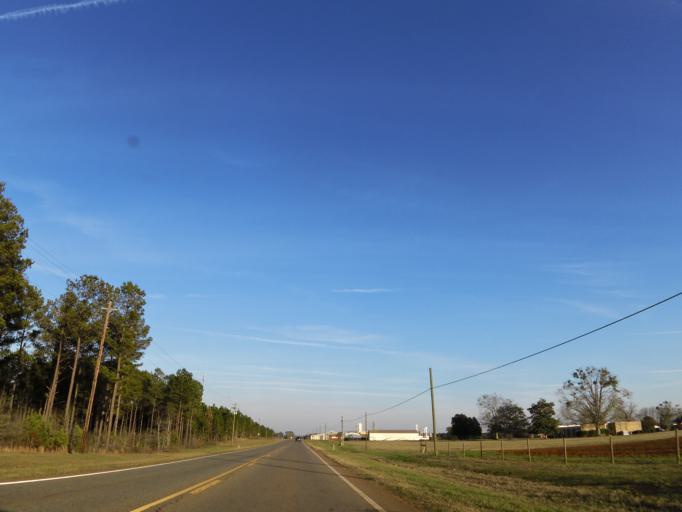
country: US
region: Georgia
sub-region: Sumter County
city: Americus
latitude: 32.0479
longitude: -84.3725
